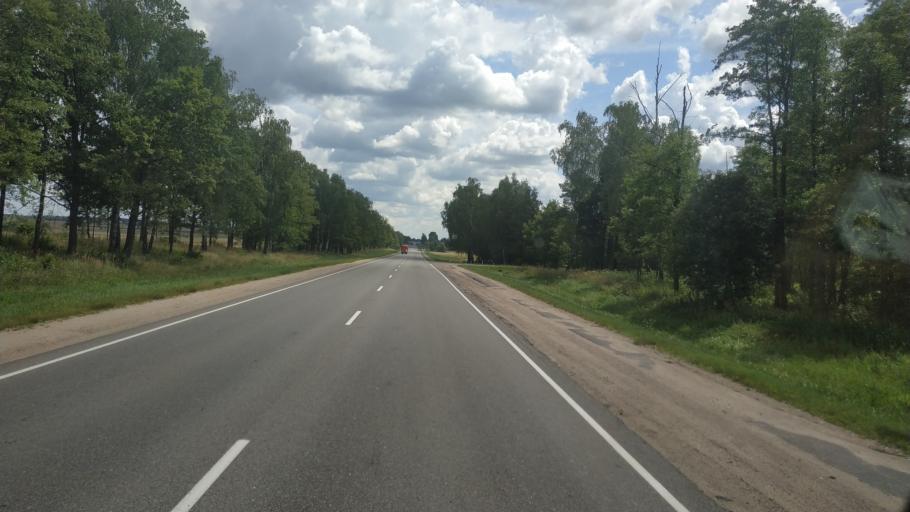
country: BY
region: Mogilev
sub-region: Mahilyowski Rayon
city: Veyno
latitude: 53.8193
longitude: 30.4386
